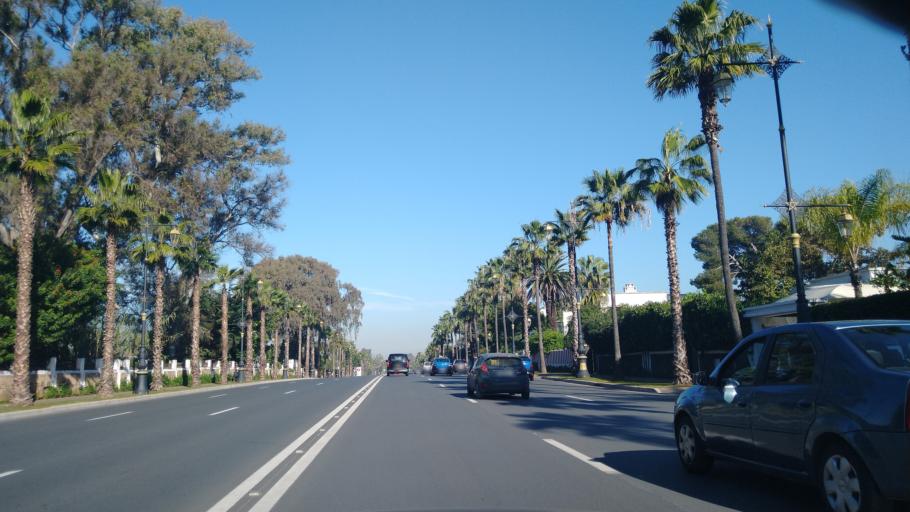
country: MA
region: Rabat-Sale-Zemmour-Zaer
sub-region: Rabat
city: Rabat
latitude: 33.9959
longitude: -6.8274
